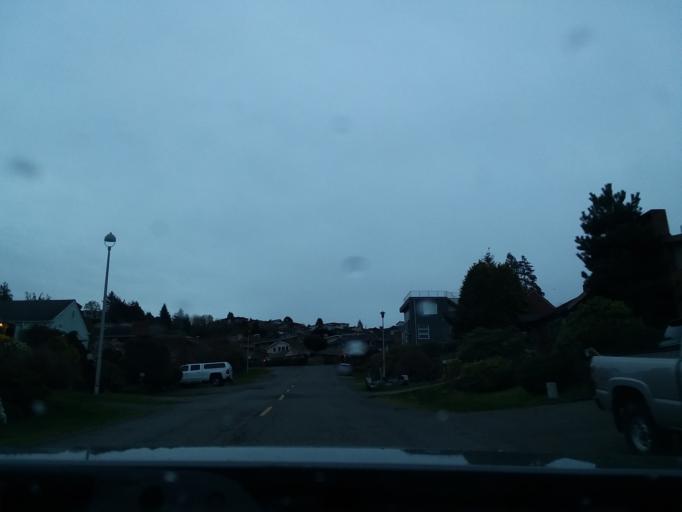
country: US
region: Washington
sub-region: King County
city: Shoreline
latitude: 47.7011
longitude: -122.3888
